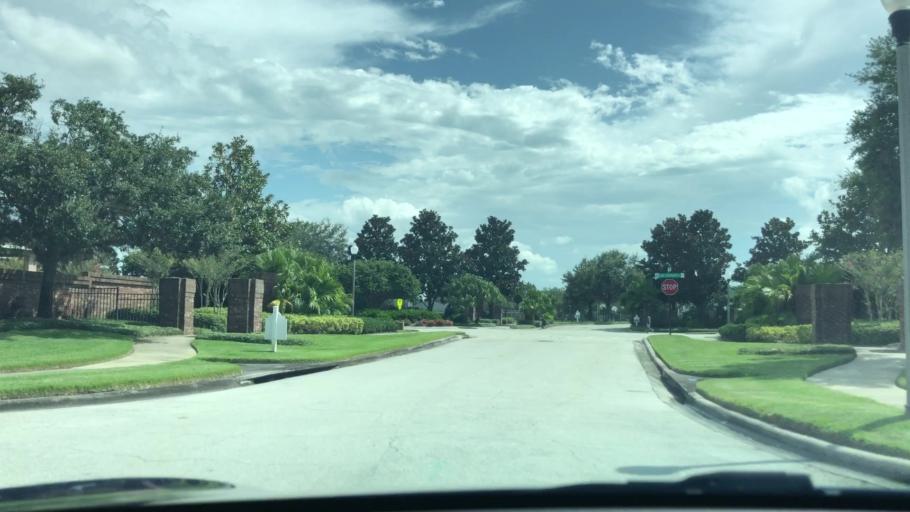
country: US
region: Florida
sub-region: Orange County
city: Conway
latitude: 28.4749
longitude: -81.2692
